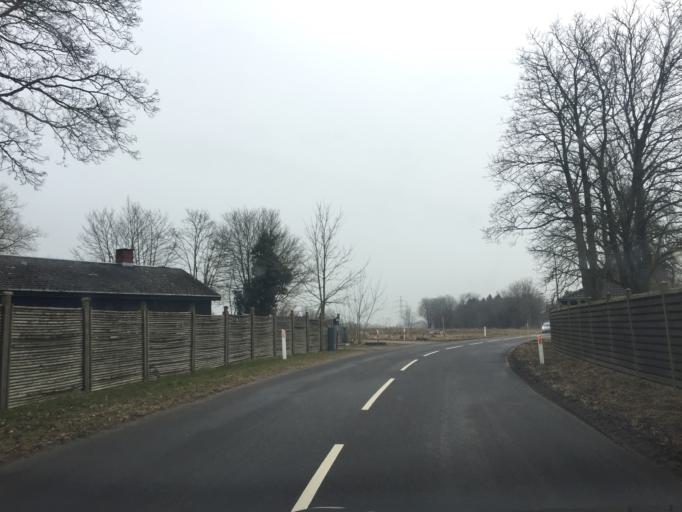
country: DK
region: Capital Region
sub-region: Hoje-Taastrup Kommune
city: Flong
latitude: 55.6433
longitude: 12.2219
